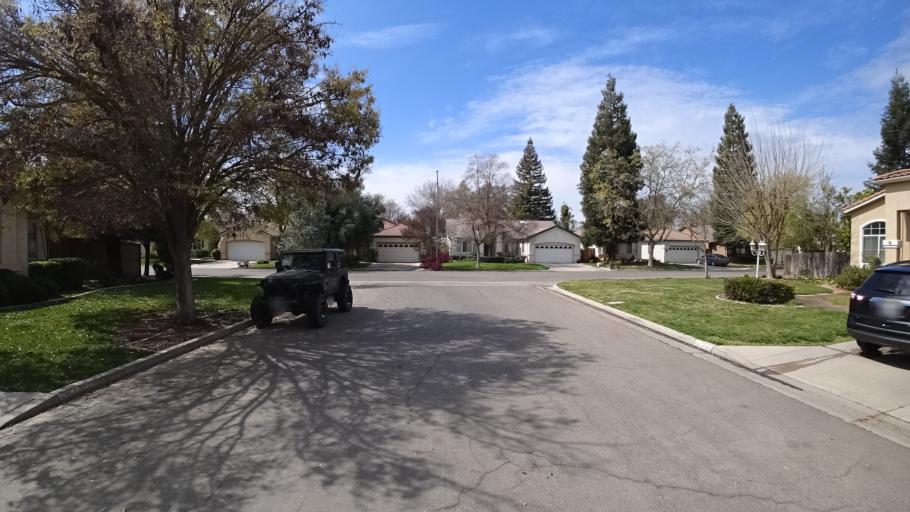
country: US
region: California
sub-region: Fresno County
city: Biola
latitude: 36.8425
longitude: -119.9048
